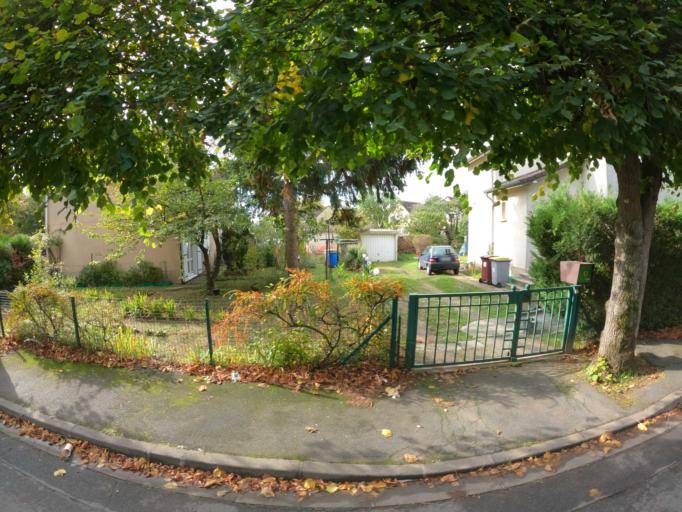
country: FR
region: Ile-de-France
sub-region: Departement de Seine-et-Marne
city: Brou-sur-Chantereine
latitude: 48.8823
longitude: 2.6226
